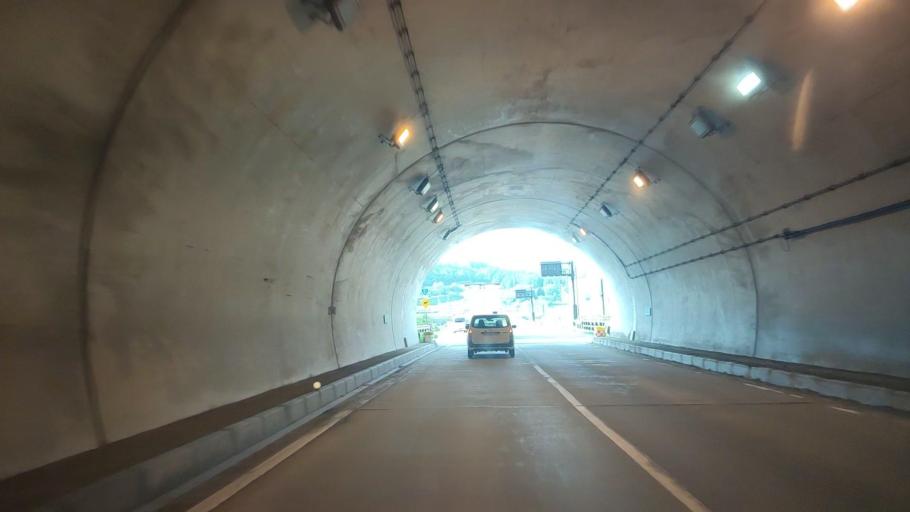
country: JP
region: Toyama
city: Yatsuomachi-higashikumisaka
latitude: 36.5312
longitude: 137.2262
